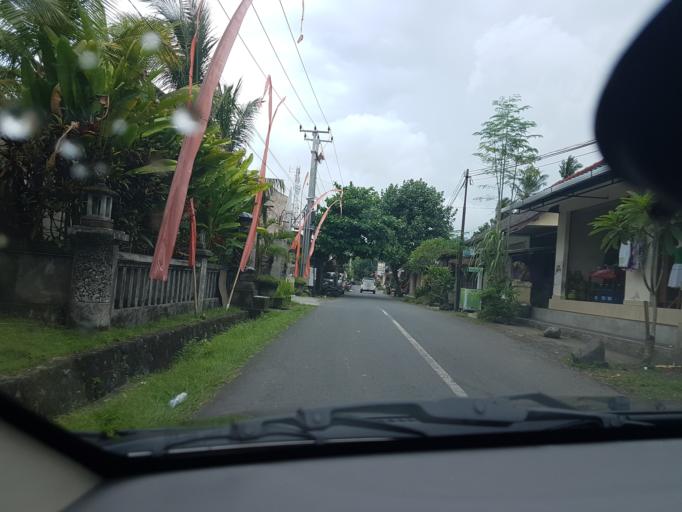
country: ID
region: Bali
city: Banjar Pande
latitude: -8.5041
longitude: 115.2449
